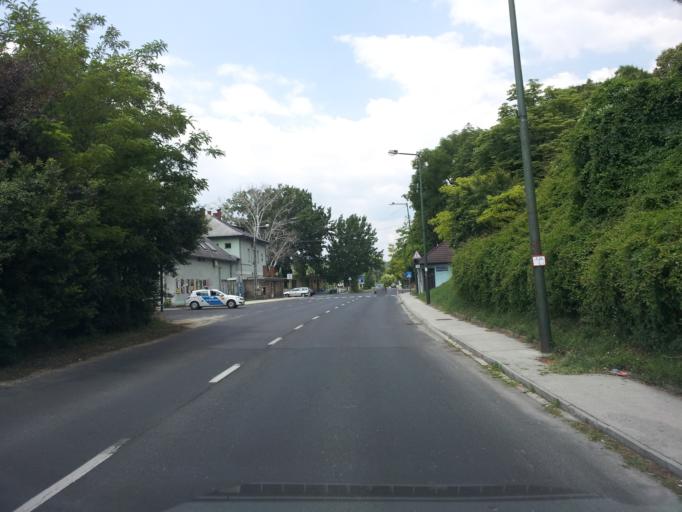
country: HU
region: Veszprem
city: Balatonalmadi
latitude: 47.0595
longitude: 18.0436
